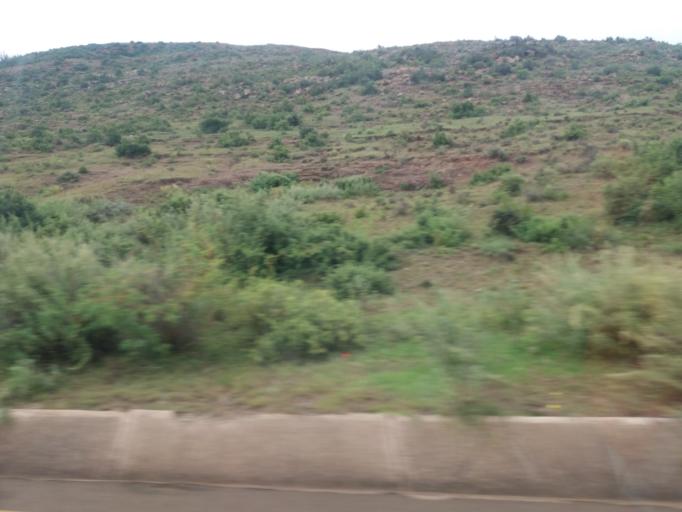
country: LS
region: Berea
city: Teyateyaneng
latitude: -29.3242
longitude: 27.7597
